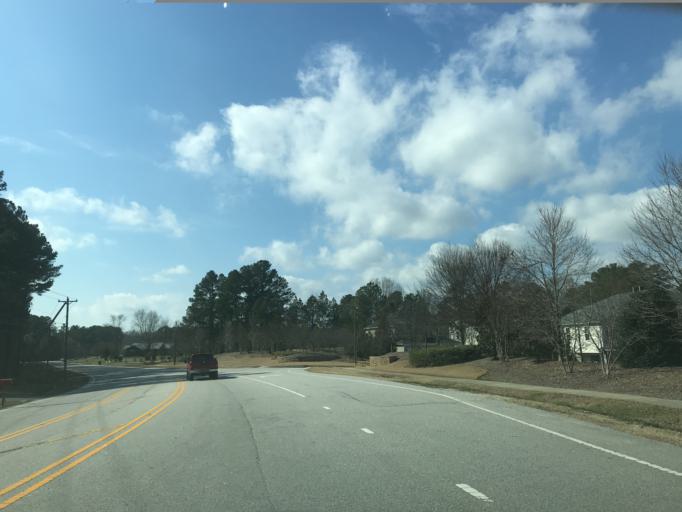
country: US
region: North Carolina
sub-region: Durham County
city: Gorman
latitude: 35.9571
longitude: -78.8245
